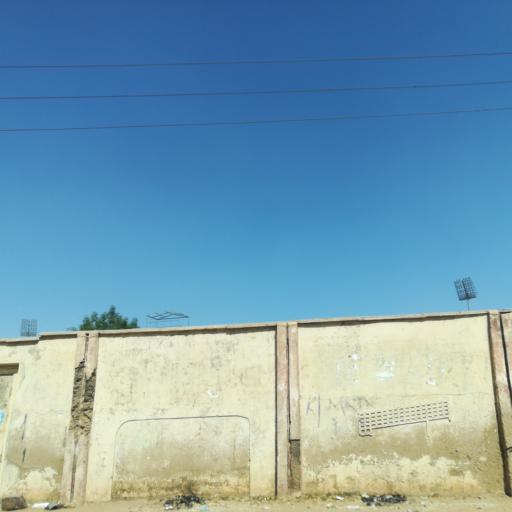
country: NG
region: Kano
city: Kano
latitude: 11.9988
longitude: 8.5286
